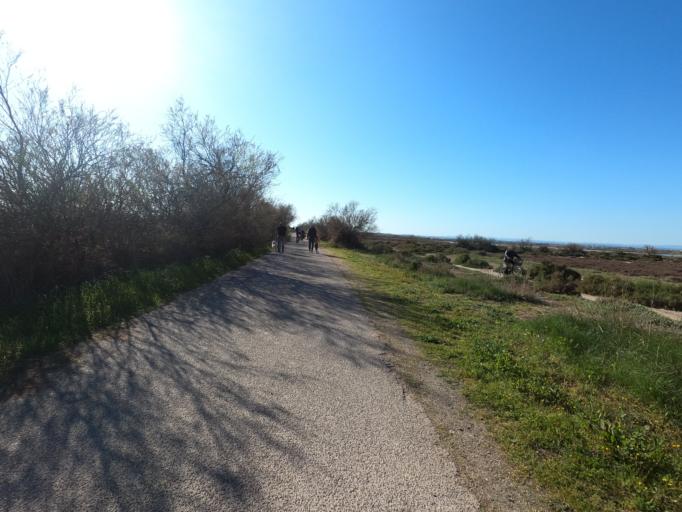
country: FR
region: Languedoc-Roussillon
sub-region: Departement de l'Herault
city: Palavas-les-Flots
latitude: 43.5360
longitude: 3.9141
